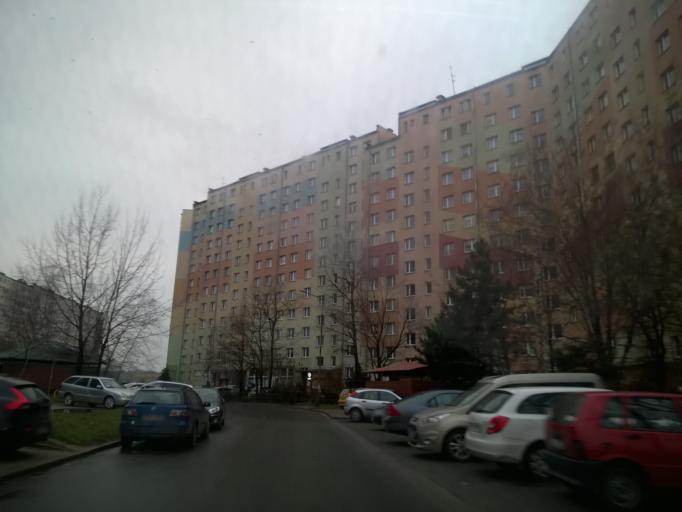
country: PL
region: Lower Silesian Voivodeship
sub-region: Powiat wroclawski
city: Wroclaw
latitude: 51.0811
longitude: 17.0463
